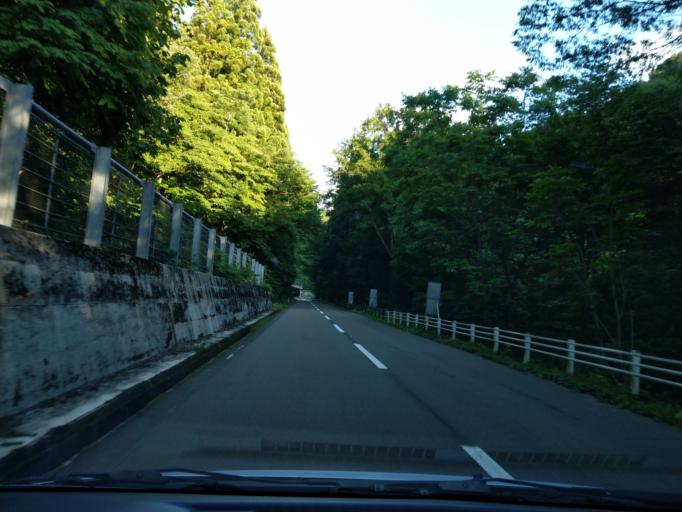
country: JP
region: Akita
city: Kakunodatemachi
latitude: 39.8744
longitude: 140.4815
